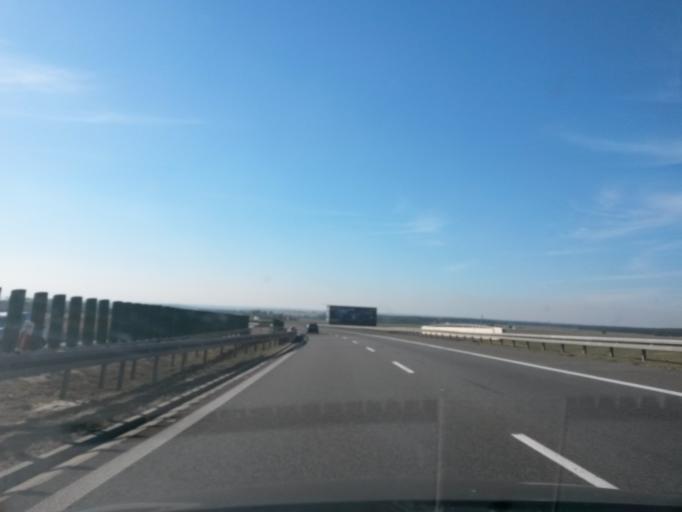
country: PL
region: Opole Voivodeship
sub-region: Powiat krapkowicki
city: Rozwadza
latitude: 50.4817
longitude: 18.1166
